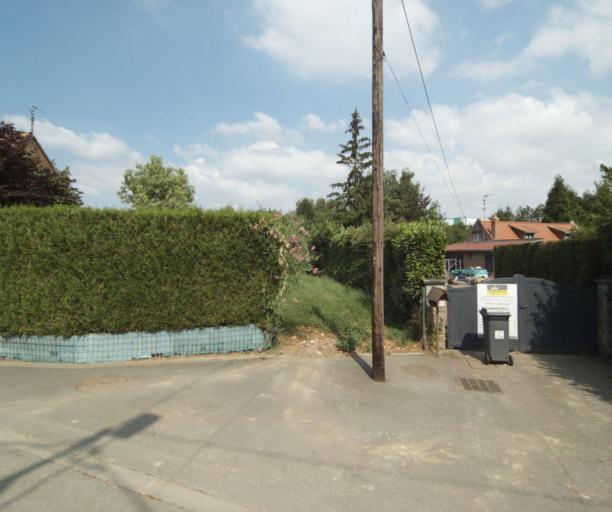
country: FR
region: Nord-Pas-de-Calais
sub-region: Departement du Nord
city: Santes
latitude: 50.5975
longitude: 2.9728
